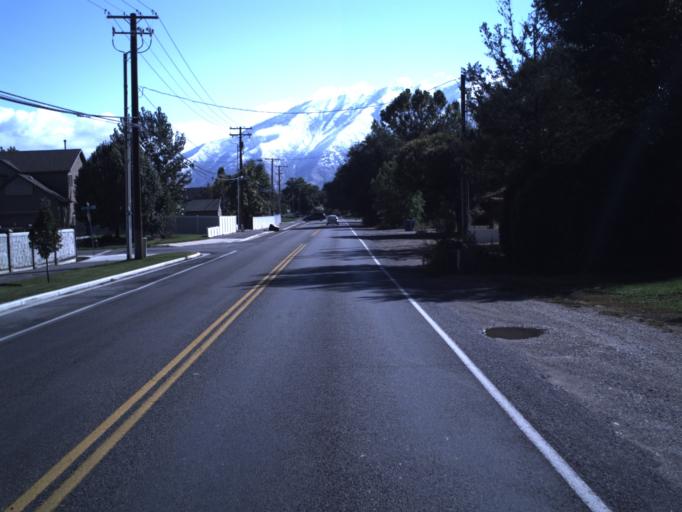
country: US
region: Utah
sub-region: Utah County
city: Spanish Fork
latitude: 40.1080
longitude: -111.6637
